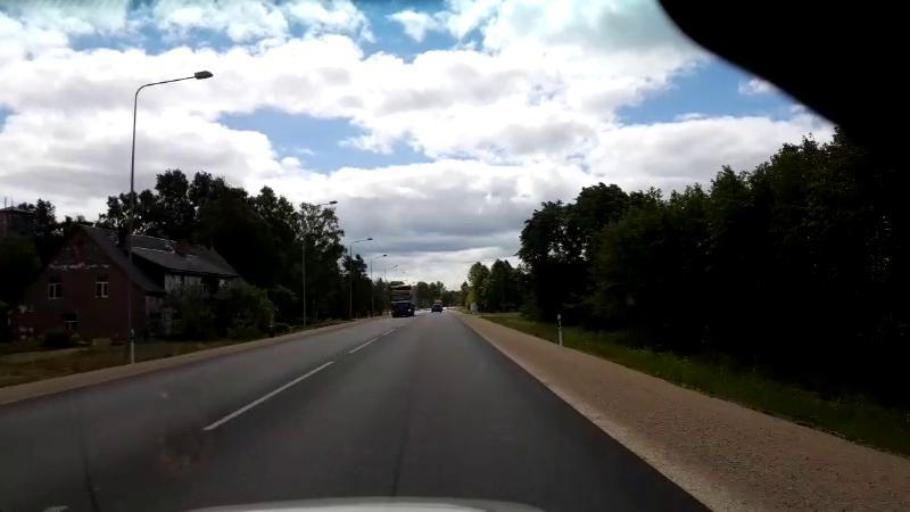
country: LV
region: Salacgrivas
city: Salacgriva
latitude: 57.7890
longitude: 24.3540
